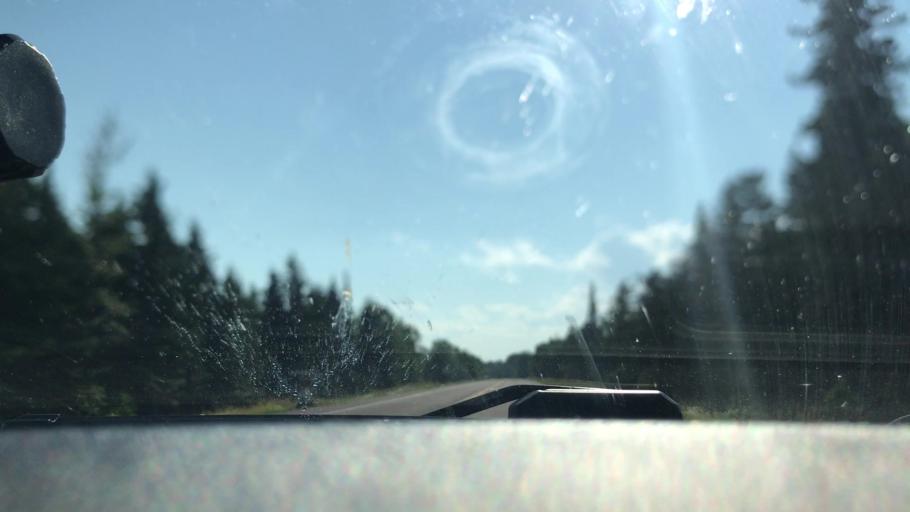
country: US
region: Minnesota
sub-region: Cook County
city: Grand Marais
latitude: 47.8277
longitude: -90.0062
